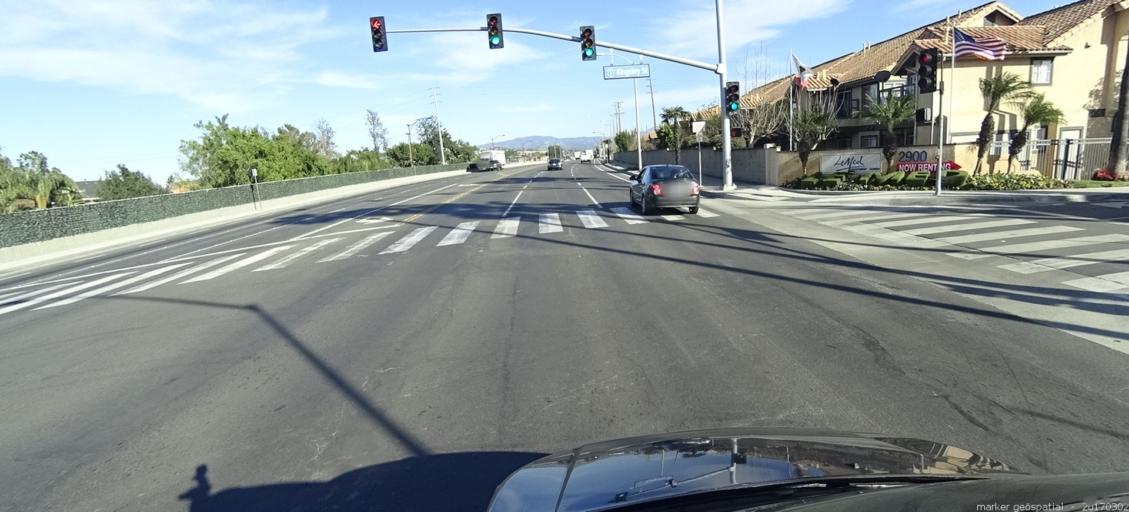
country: US
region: California
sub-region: Orange County
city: Placentia
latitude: 33.8363
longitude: -117.8673
